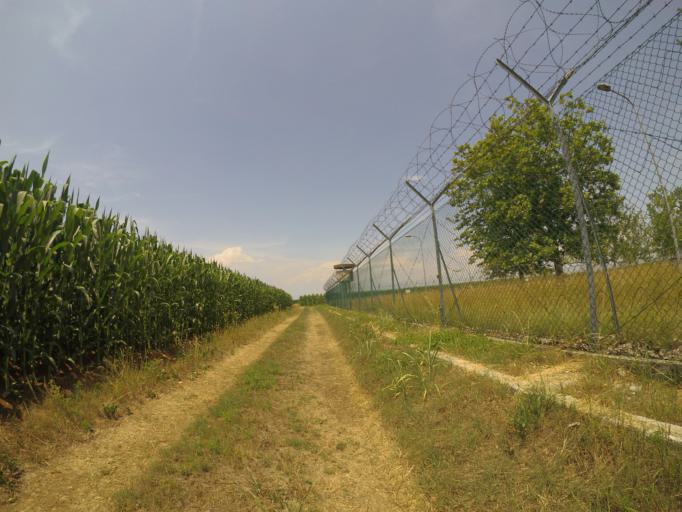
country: IT
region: Friuli Venezia Giulia
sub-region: Provincia di Udine
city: Bertiolo
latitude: 45.9555
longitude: 13.0393
